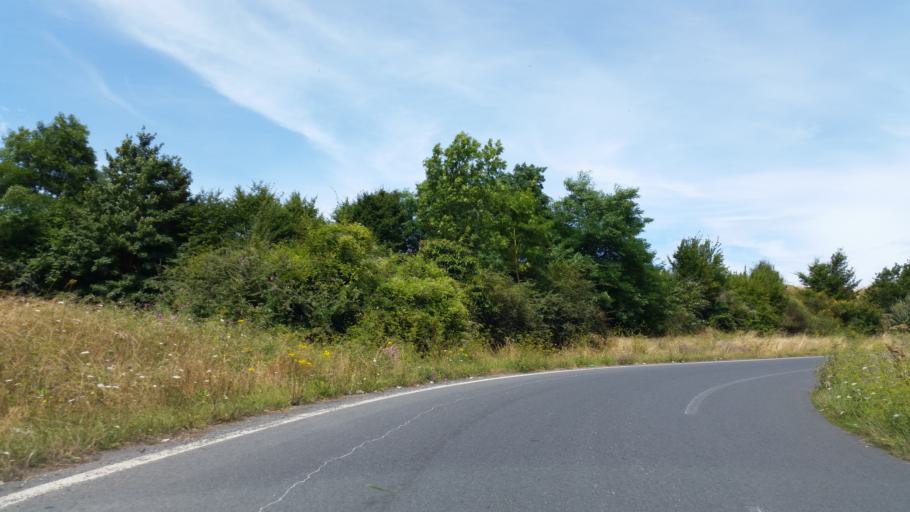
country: FR
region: Lower Normandy
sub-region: Departement du Calvados
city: Herouville-Saint-Clair
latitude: 49.2102
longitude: -0.3231
